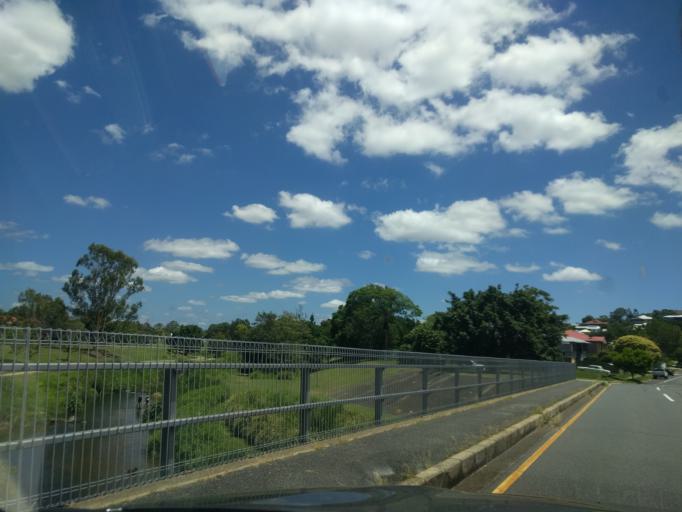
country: AU
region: Queensland
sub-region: Brisbane
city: Gordon Park
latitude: -27.4221
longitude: 153.0241
